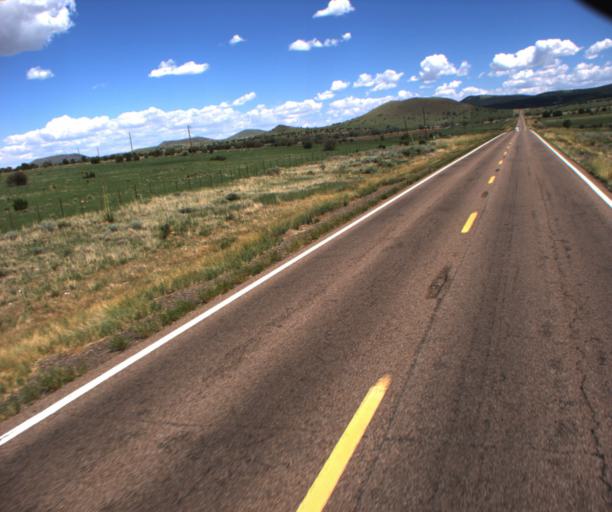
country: US
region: Arizona
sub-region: Navajo County
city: Pinetop-Lakeside
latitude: 34.2714
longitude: -109.6687
